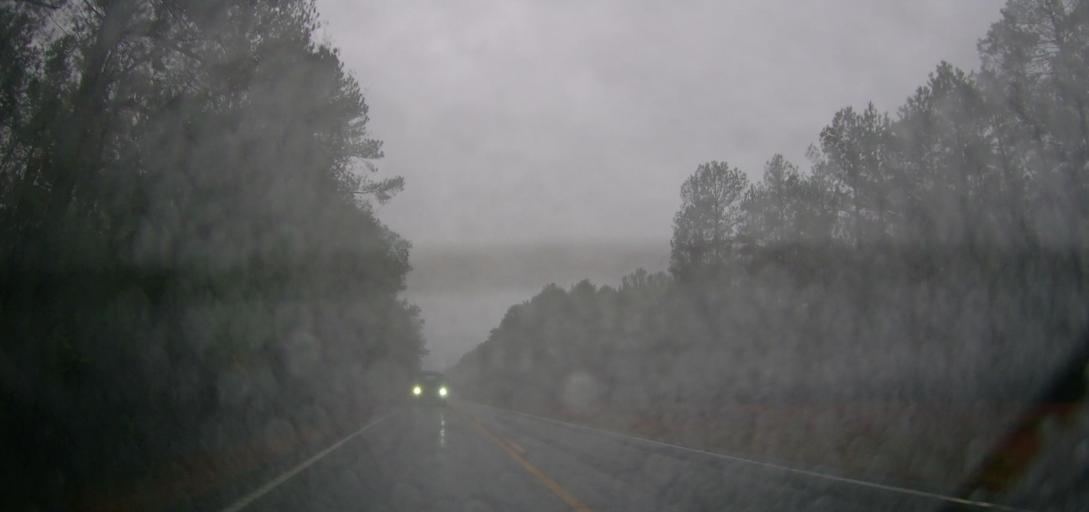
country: US
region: Georgia
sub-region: Putnam County
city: Eatonton
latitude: 33.1835
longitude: -83.4390
